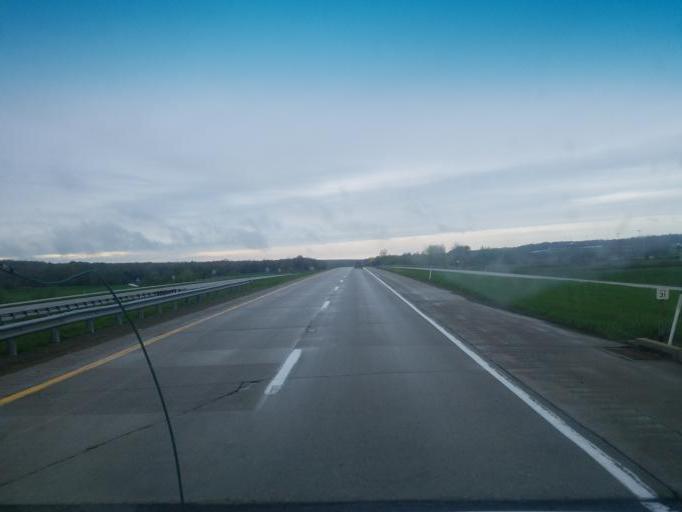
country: US
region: Pennsylvania
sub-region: Erie County
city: North East
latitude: 42.1382
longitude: -79.8223
